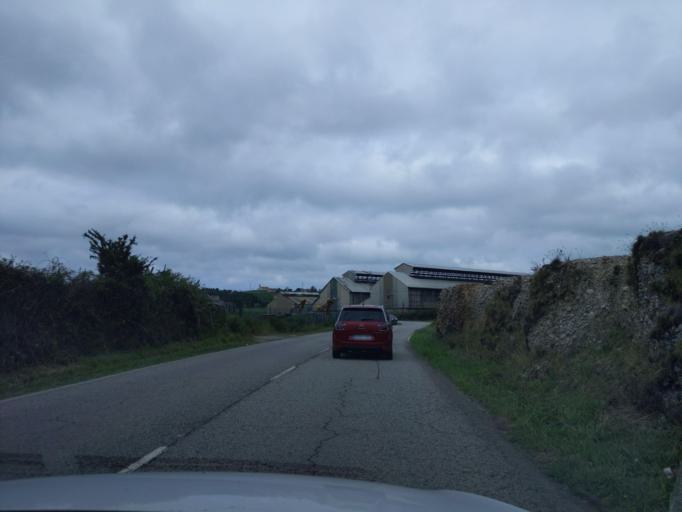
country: ES
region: Asturias
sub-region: Province of Asturias
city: Aviles
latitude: 43.5809
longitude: -5.9167
